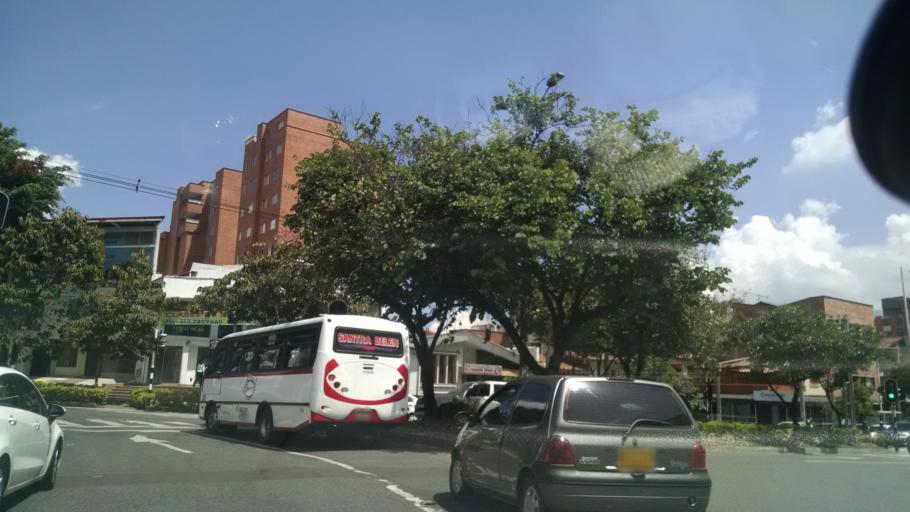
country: CO
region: Antioquia
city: Medellin
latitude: 6.2386
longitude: -75.6027
